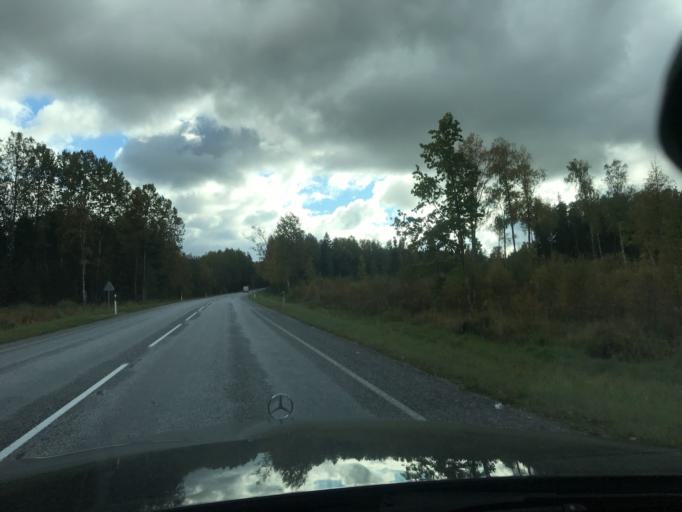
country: EE
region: Vorumaa
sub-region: Voru linn
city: Voru
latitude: 57.7260
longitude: 27.3121
